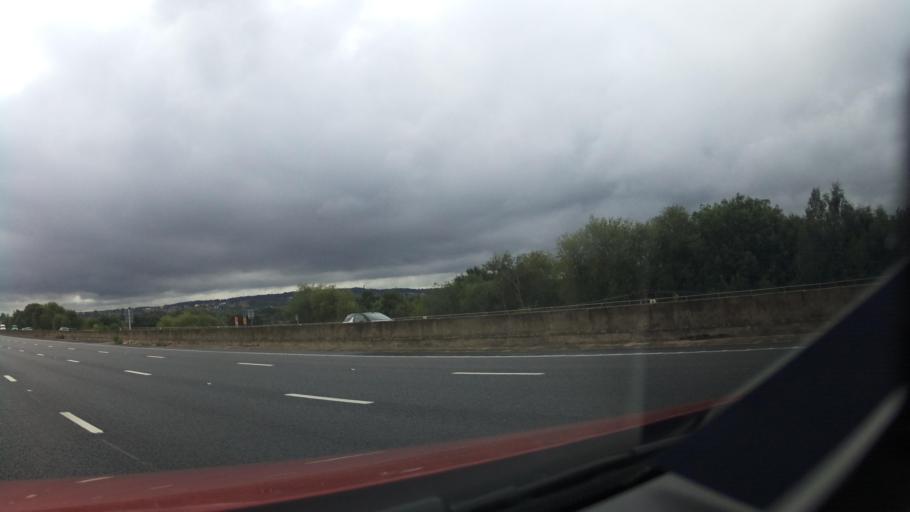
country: GB
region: England
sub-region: City and Borough of Wakefield
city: Crigglestone
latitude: 53.6656
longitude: -1.5354
